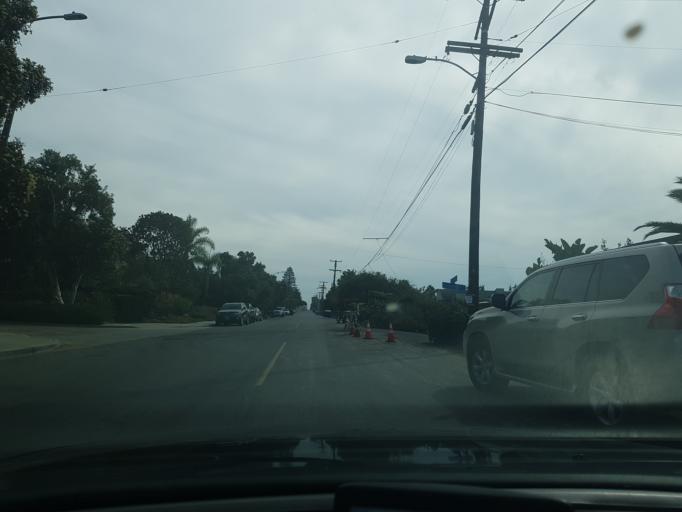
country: US
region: California
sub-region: San Diego County
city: Solana Beach
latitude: 33.0031
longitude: -117.2724
